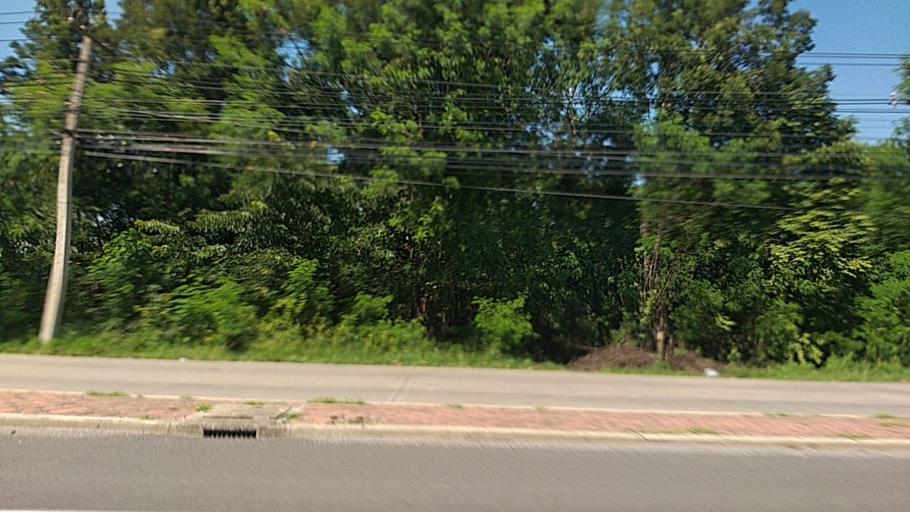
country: TH
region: Nakhon Ratchasima
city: Kham Thale So
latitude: 14.9373
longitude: 101.9903
